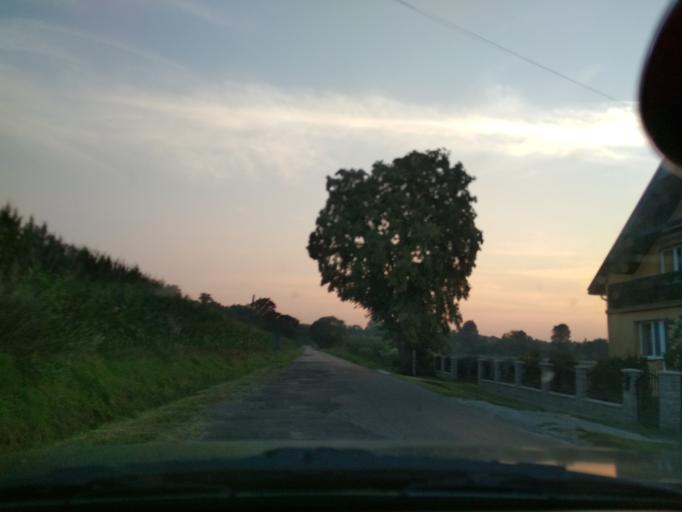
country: PL
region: Lesser Poland Voivodeship
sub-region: Powiat olkuski
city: Wolbrom
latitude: 50.4579
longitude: 19.7945
